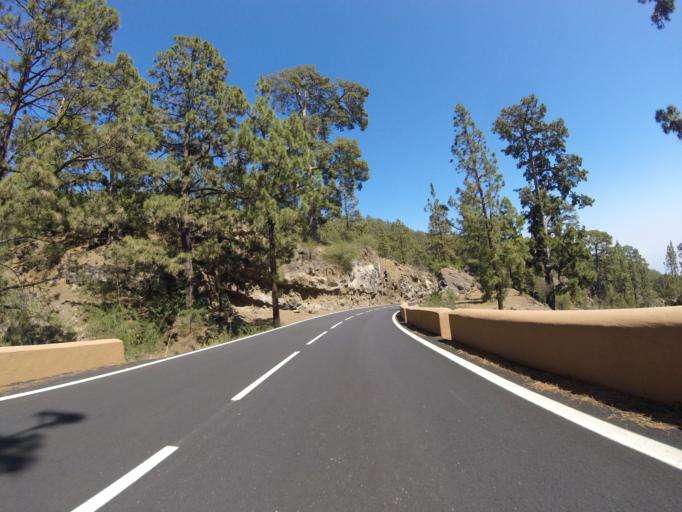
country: ES
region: Canary Islands
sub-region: Provincia de Santa Cruz de Tenerife
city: Vilaflor
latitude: 28.1751
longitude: -16.6392
